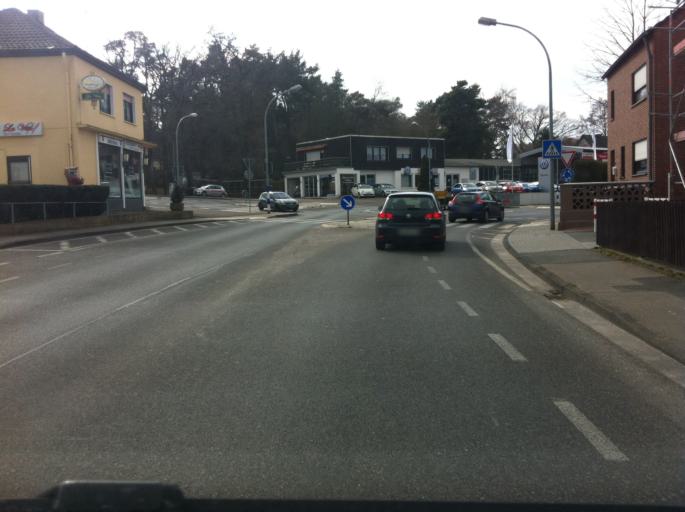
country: DE
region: North Rhine-Westphalia
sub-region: Regierungsbezirk Koln
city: Mechernich
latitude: 50.5878
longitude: 6.6510
